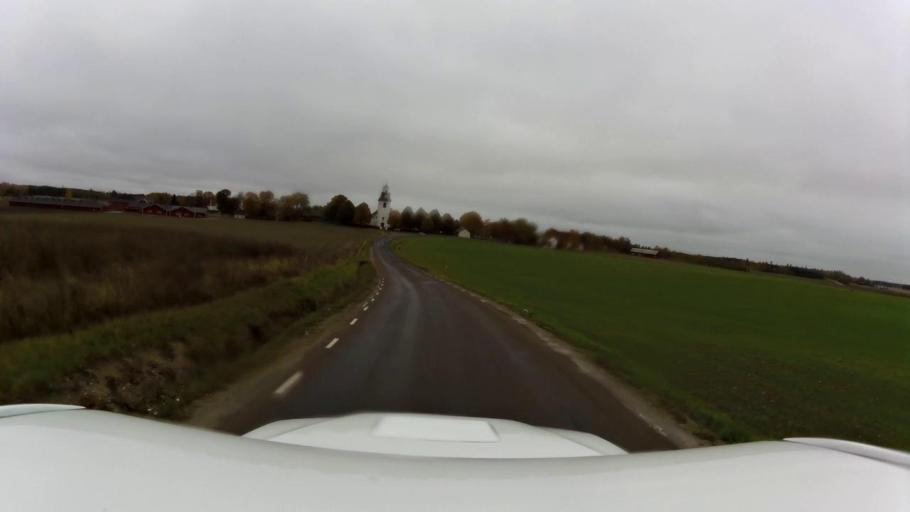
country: SE
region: OEstergoetland
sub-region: Linkopings Kommun
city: Ekangen
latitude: 58.4507
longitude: 15.7066
